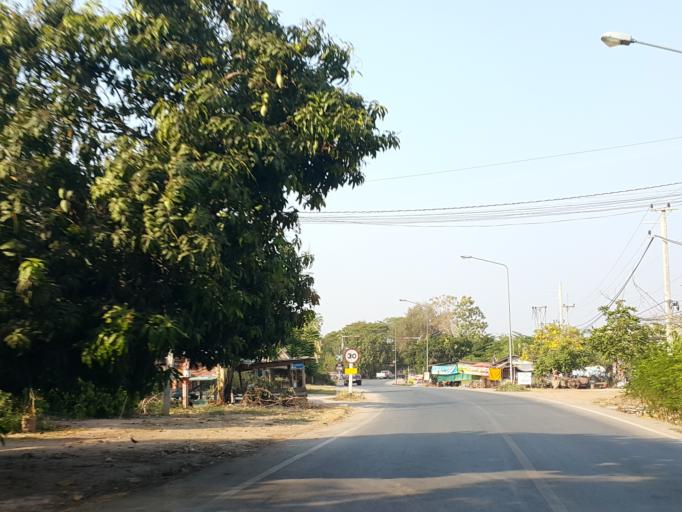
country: TH
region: Phitsanulok
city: Phrom Phiram
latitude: 17.0781
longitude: 100.1785
